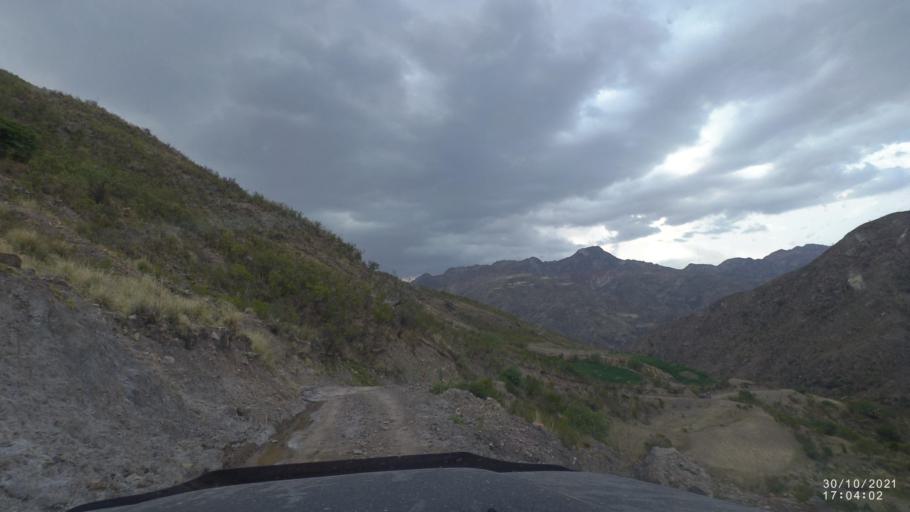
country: BO
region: Cochabamba
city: Colchani
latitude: -17.5680
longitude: -66.6313
